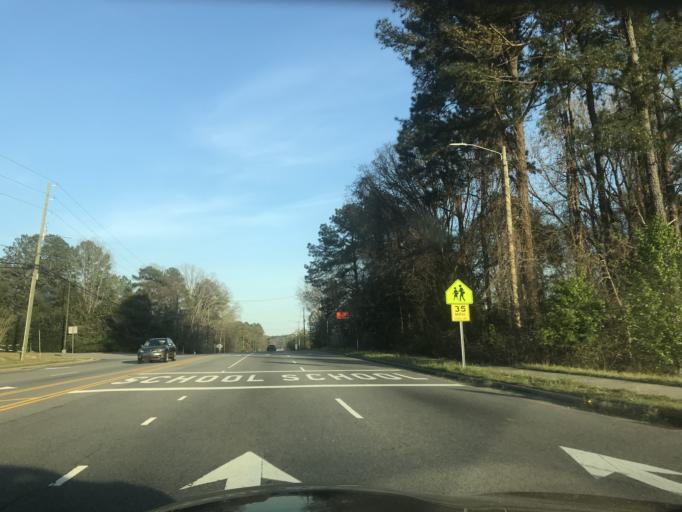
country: US
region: North Carolina
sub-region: Wake County
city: Garner
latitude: 35.7458
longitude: -78.5847
